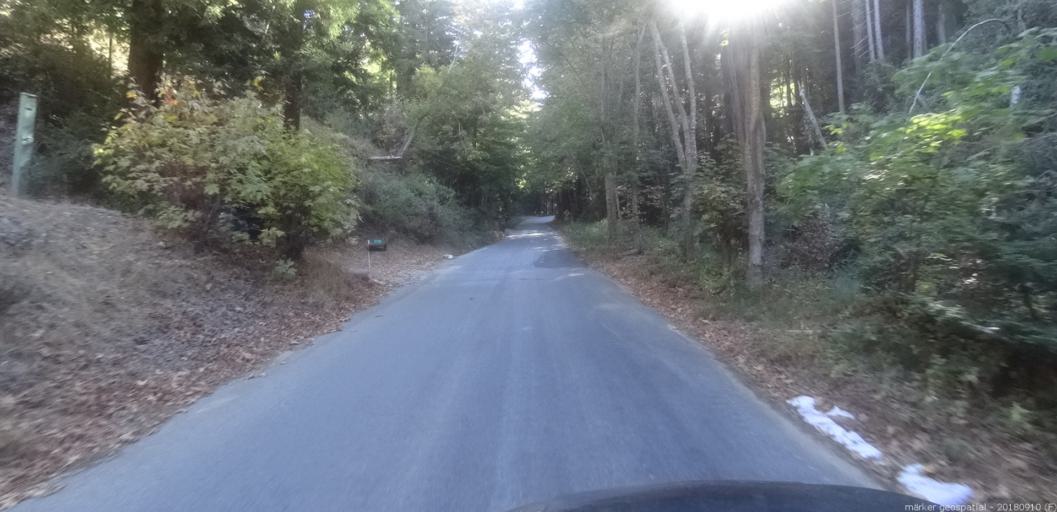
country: US
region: California
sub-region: Monterey County
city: Carmel Valley Village
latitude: 36.3896
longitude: -121.8732
